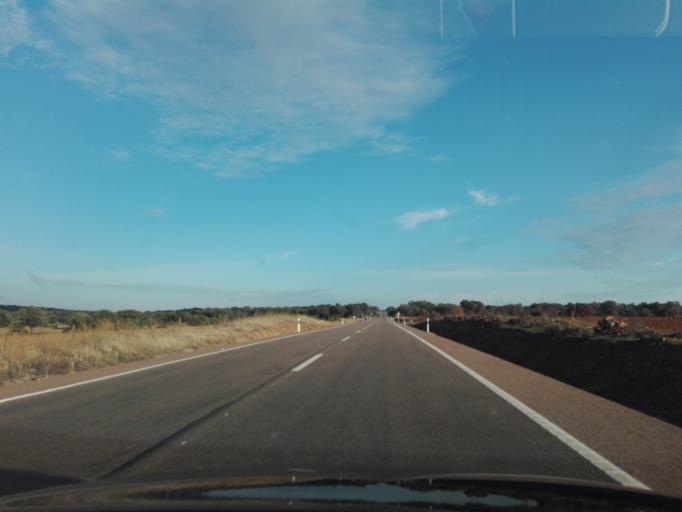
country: ES
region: Extremadura
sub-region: Provincia de Badajoz
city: Usagre
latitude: 38.3702
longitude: -6.2465
